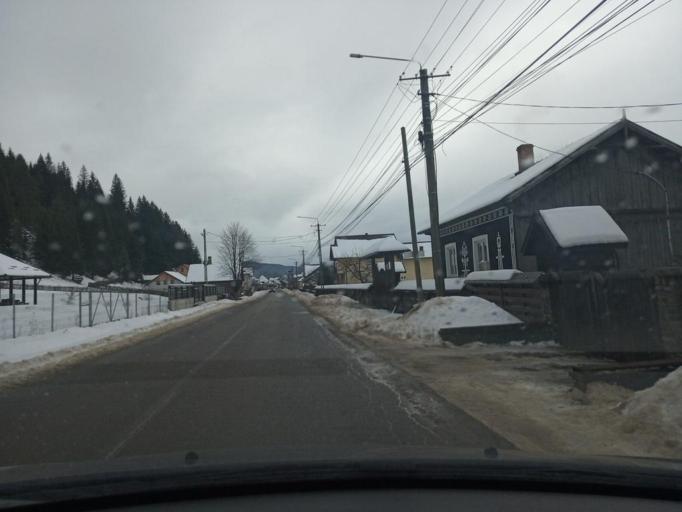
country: RO
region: Suceava
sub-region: Comuna Manastirea Humorului
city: Manastirea Humorului
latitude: 47.5871
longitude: 25.8694
